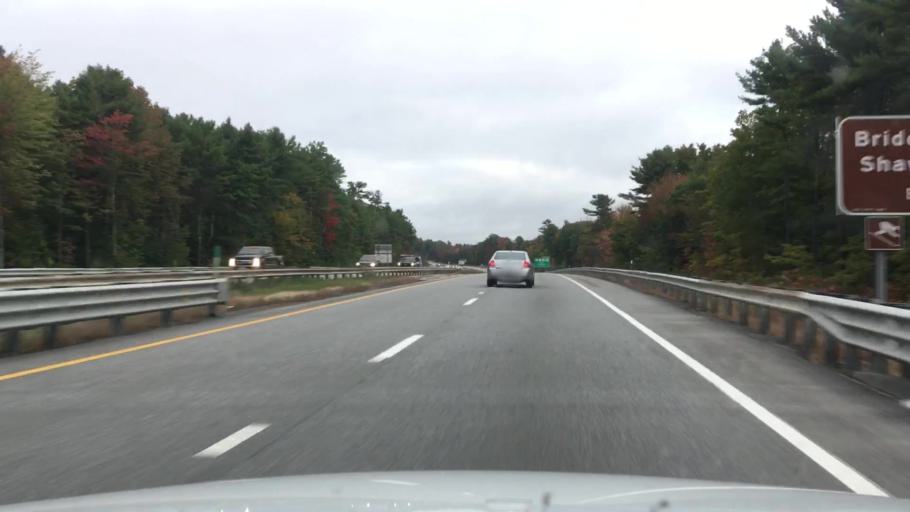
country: US
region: Maine
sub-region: Cumberland County
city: Cumberland Center
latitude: 43.8499
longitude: -70.3230
